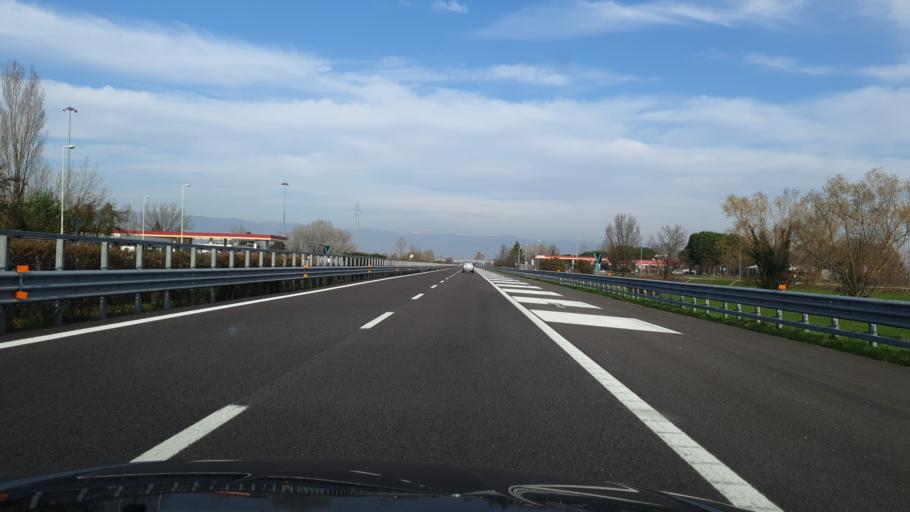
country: IT
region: Veneto
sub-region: Provincia di Vicenza
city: Vigardolo
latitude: 45.5923
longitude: 11.5991
